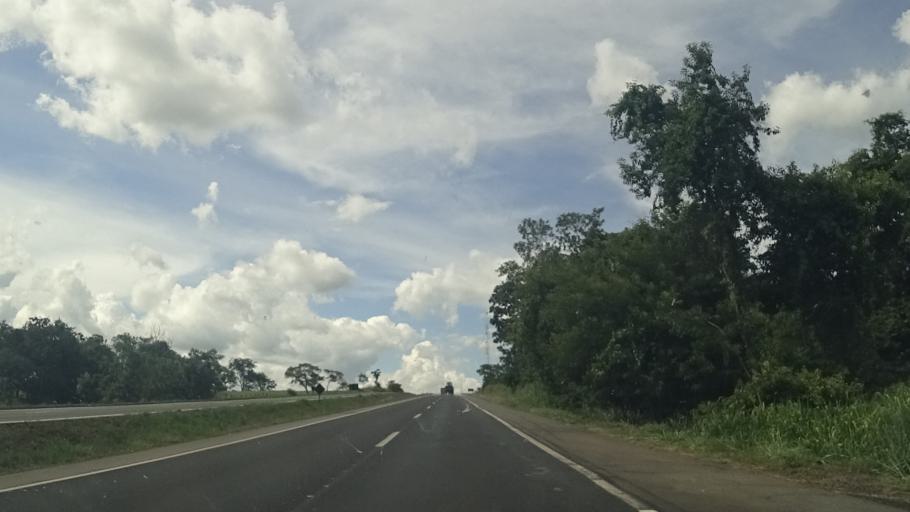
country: BR
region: Goias
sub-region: Piracanjuba
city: Piracanjuba
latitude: -17.2963
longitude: -49.2341
